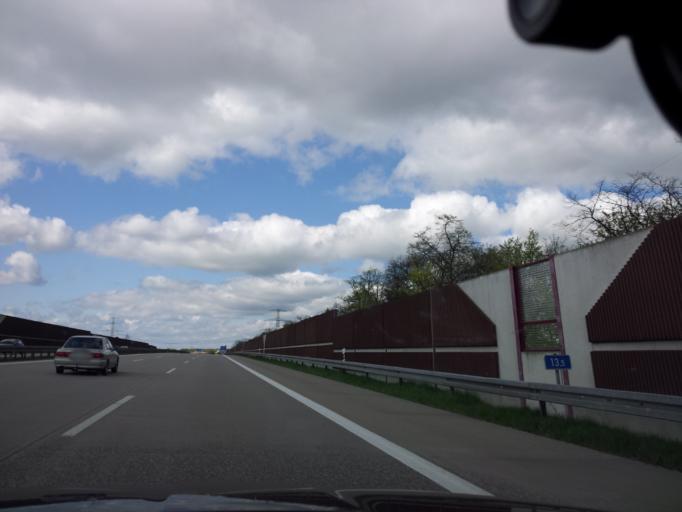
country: DE
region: Brandenburg
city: Neuenhagen
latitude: 52.5351
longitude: 13.7028
